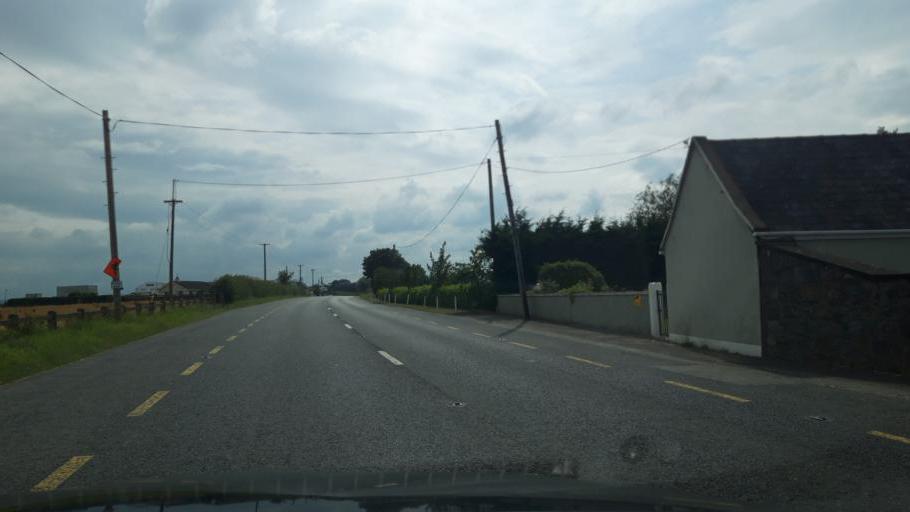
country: IE
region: Leinster
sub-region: Kildare
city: Athy
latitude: 52.9813
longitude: -7.0049
